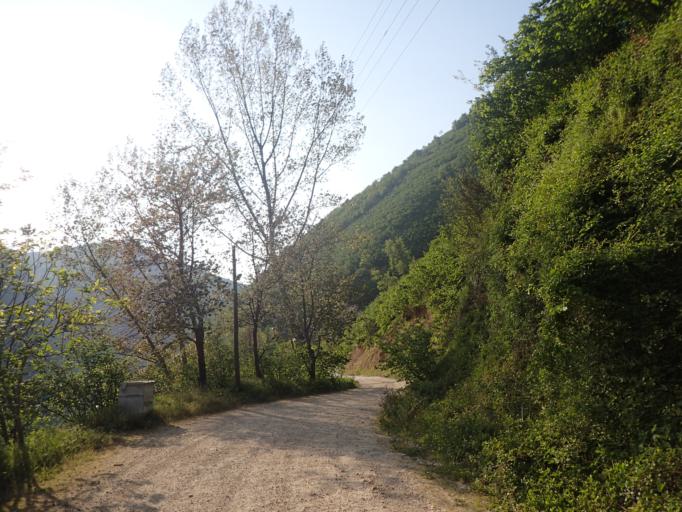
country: TR
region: Ordu
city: Kabaduz
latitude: 40.7912
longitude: 37.8812
